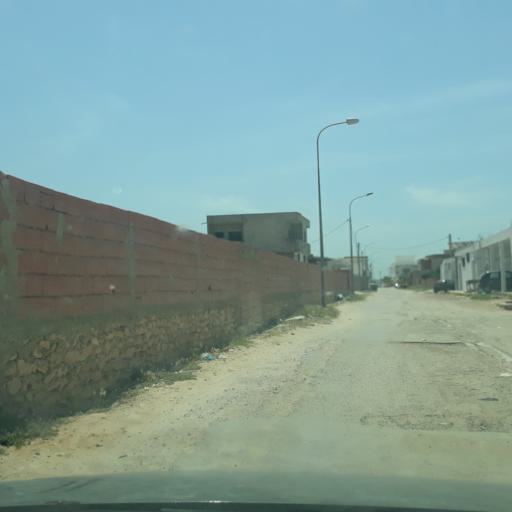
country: TN
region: Safaqis
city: Al Qarmadah
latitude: 34.8255
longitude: 10.7791
